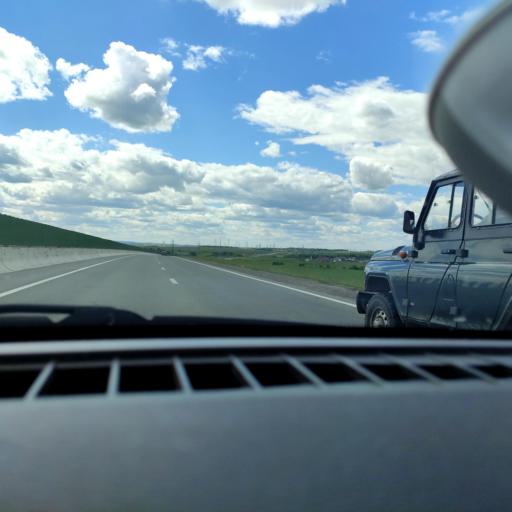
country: RU
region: Perm
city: Ferma
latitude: 57.9348
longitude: 56.3569
